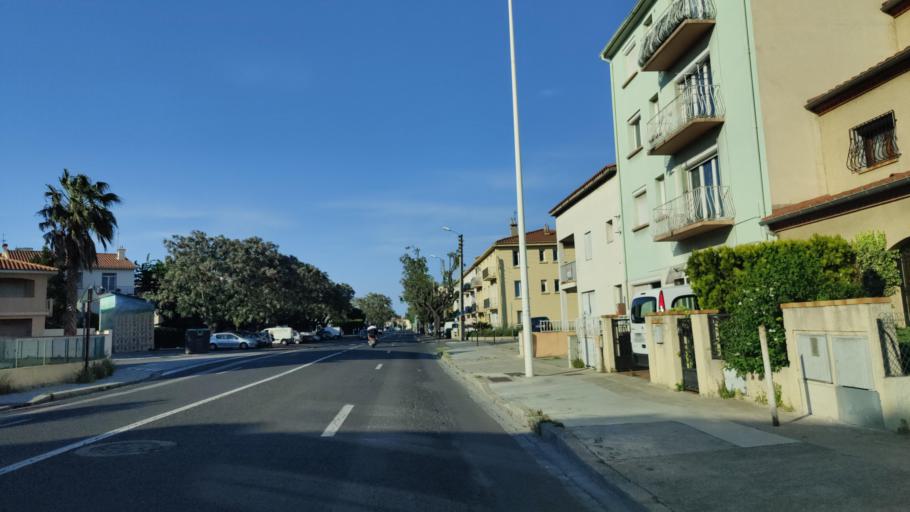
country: FR
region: Languedoc-Roussillon
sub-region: Departement des Pyrenees-Orientales
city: Perpignan
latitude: 42.7133
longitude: 2.8855
